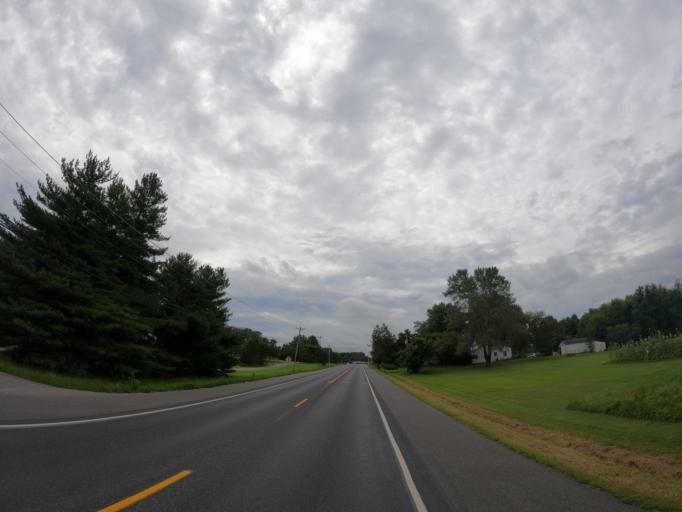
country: US
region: Maryland
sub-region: Saint Mary's County
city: California
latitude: 38.2288
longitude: -76.5191
